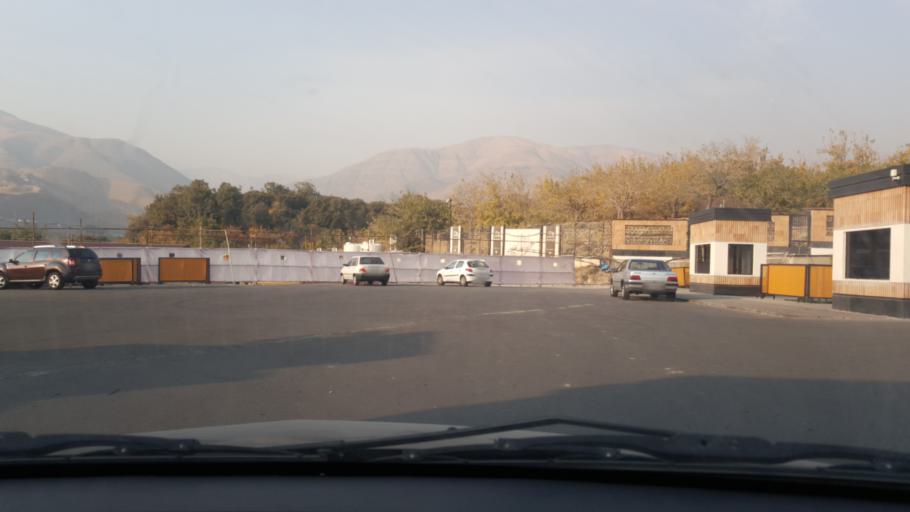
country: IR
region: Tehran
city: Tajrish
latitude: 35.7573
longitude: 51.2693
